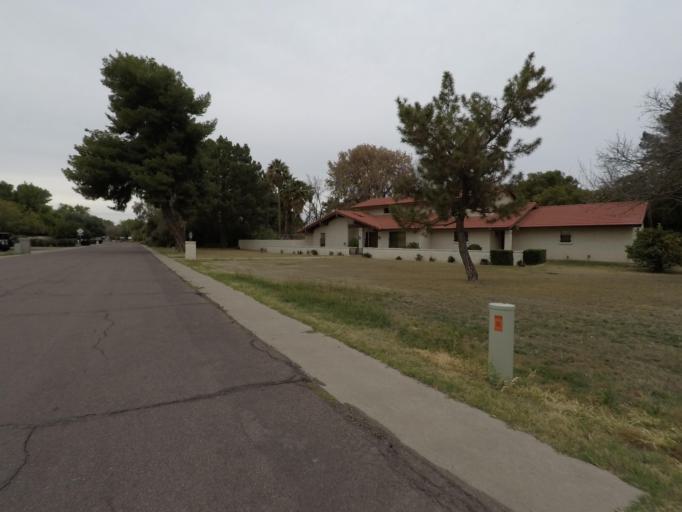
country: US
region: Arizona
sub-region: Maricopa County
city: Guadalupe
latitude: 33.3383
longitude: -111.9214
